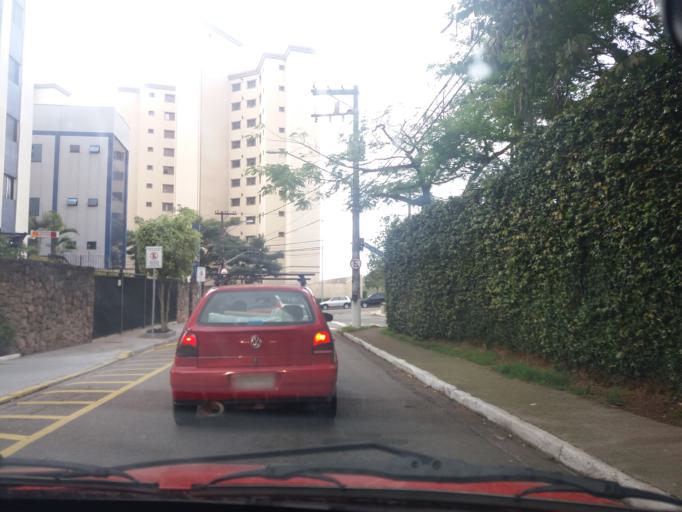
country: BR
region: Sao Paulo
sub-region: Taboao Da Serra
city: Taboao da Serra
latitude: -23.6104
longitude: -46.7346
